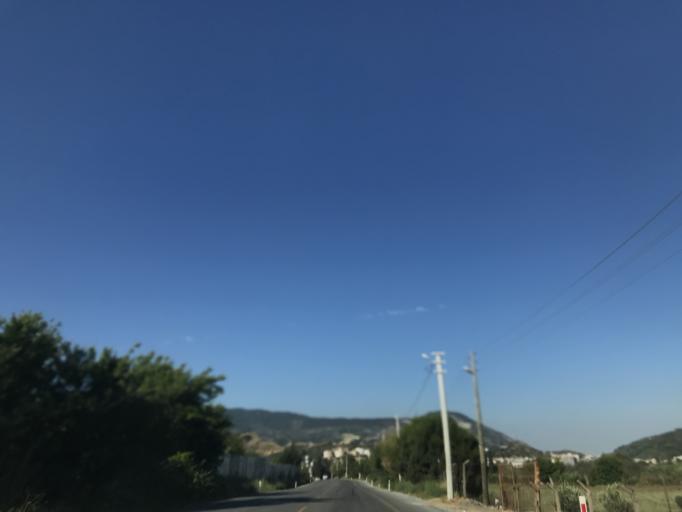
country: TR
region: Aydin
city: Soeke
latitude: 37.7577
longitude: 27.3712
